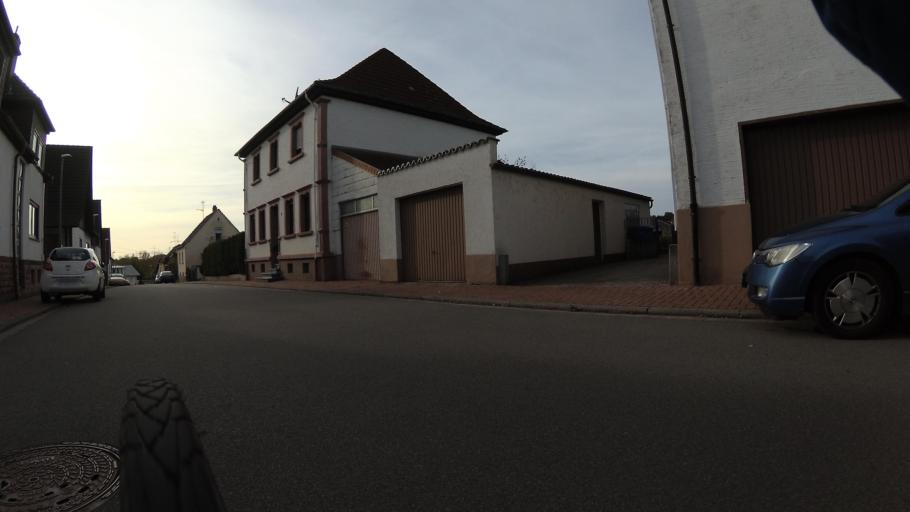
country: DE
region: Rheinland-Pfalz
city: Ramstein-Miesenbach
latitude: 49.4568
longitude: 7.5584
